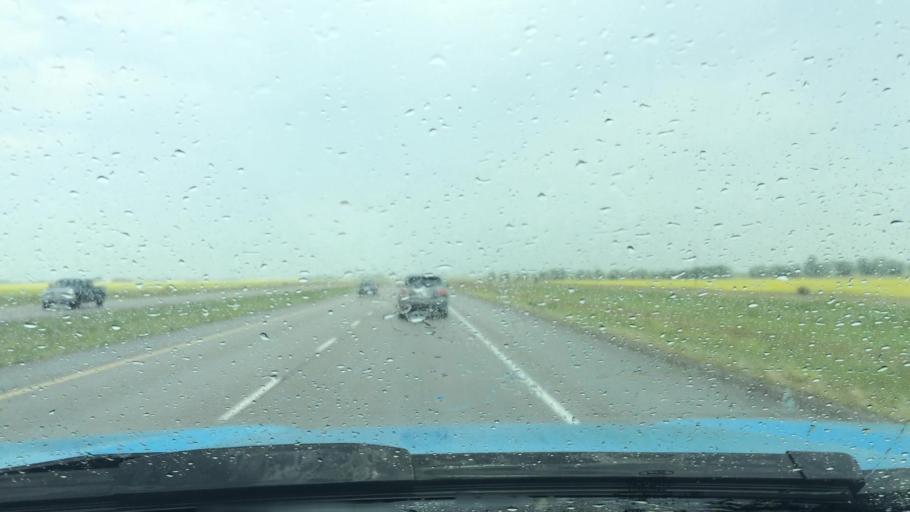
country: CA
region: Alberta
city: Carstairs
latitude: 51.6145
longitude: -114.0253
